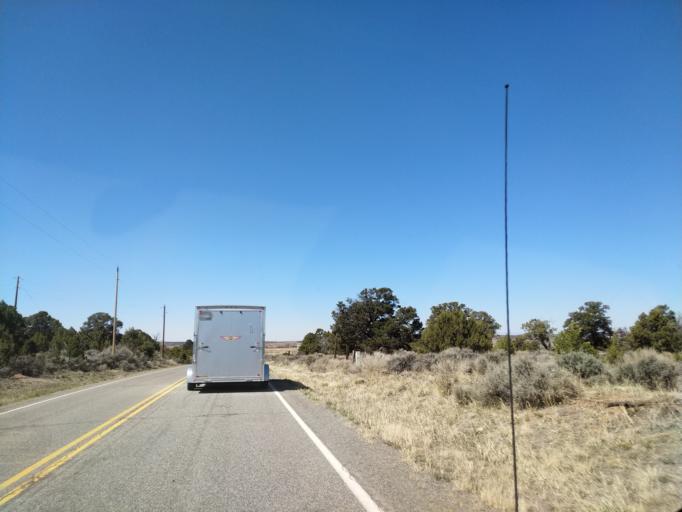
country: US
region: Colorado
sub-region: Mesa County
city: Redlands
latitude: 38.9939
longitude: -108.7272
